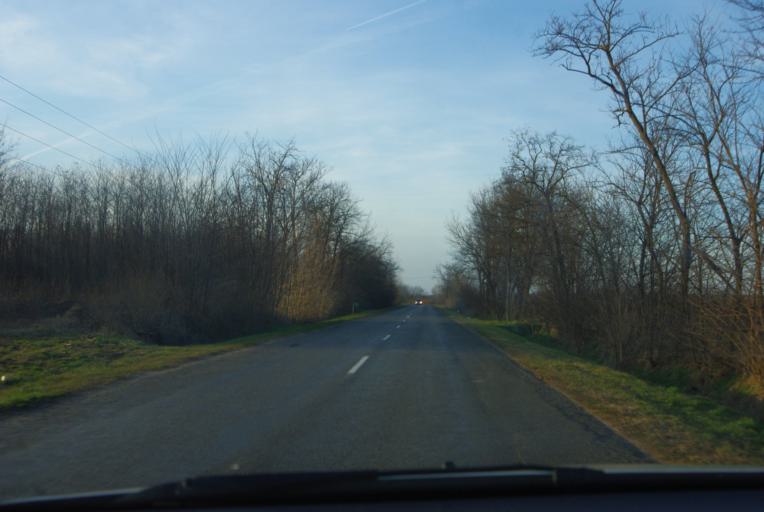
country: HU
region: Tolna
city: Bolcske
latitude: 46.7646
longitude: 18.9571
